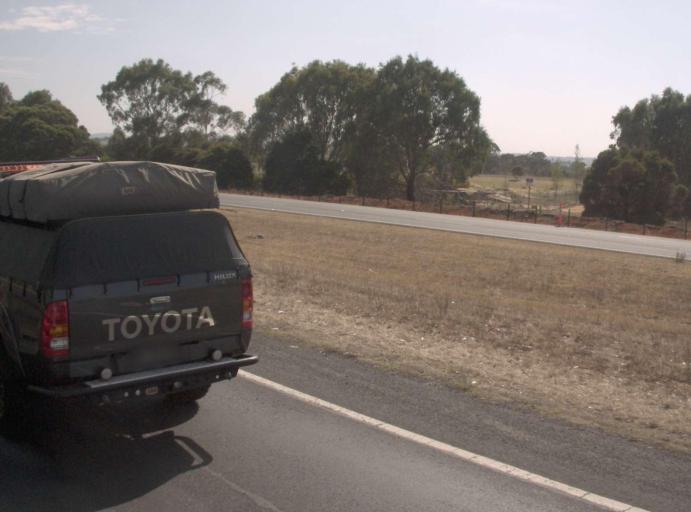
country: AU
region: Victoria
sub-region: Casey
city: Hampton Park
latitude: -38.0216
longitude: 145.2477
